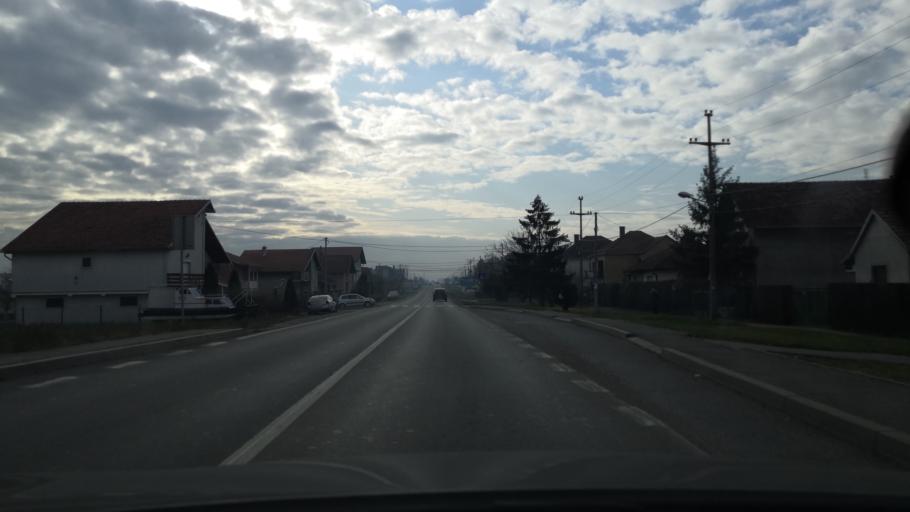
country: RS
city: Ugrinovci
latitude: 44.8698
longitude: 20.2041
